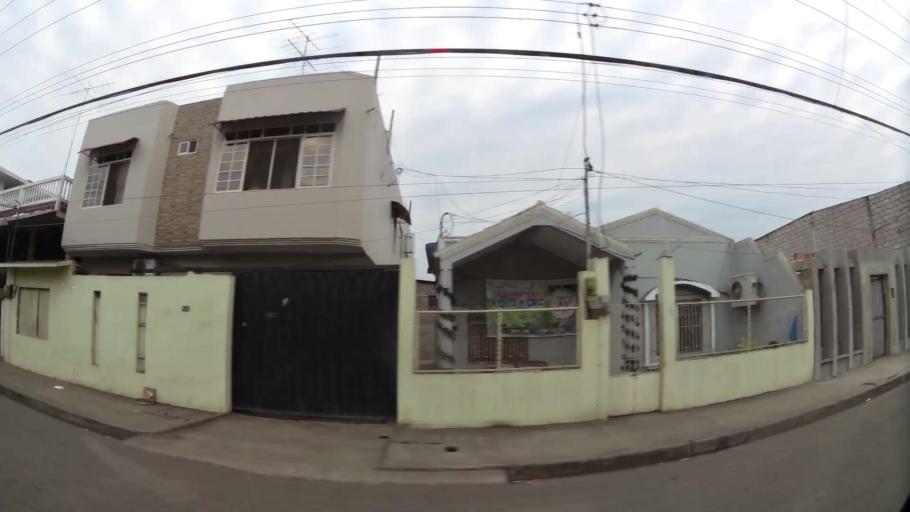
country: EC
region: El Oro
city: Machala
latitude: -3.2664
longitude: -79.9402
